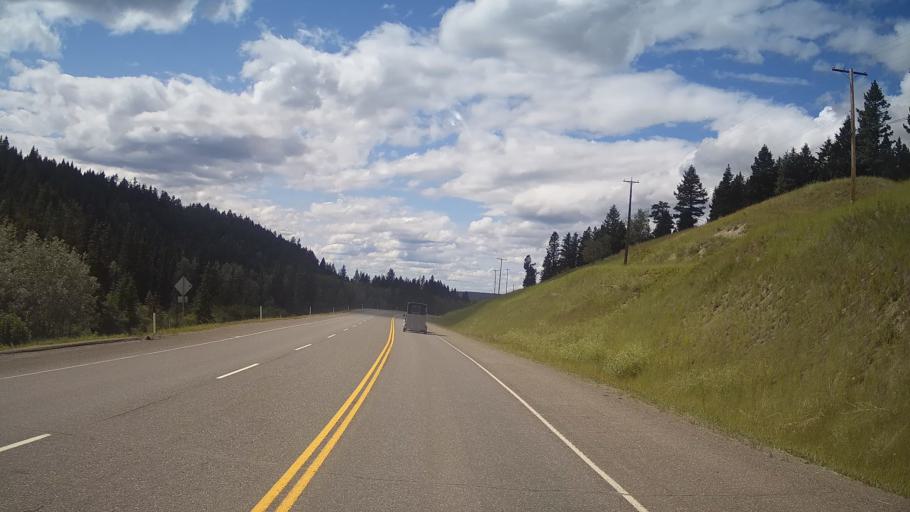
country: CA
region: British Columbia
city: Williams Lake
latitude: 51.7581
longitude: -121.3689
